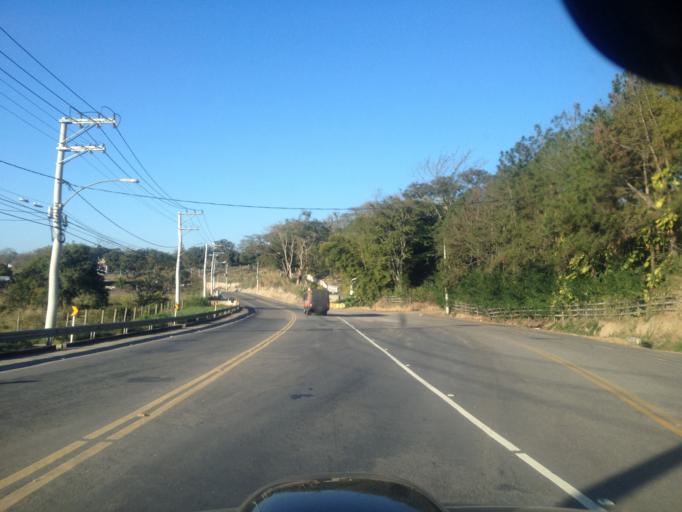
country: BR
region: Rio de Janeiro
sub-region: Porto Real
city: Porto Real
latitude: -22.4224
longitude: -44.2786
